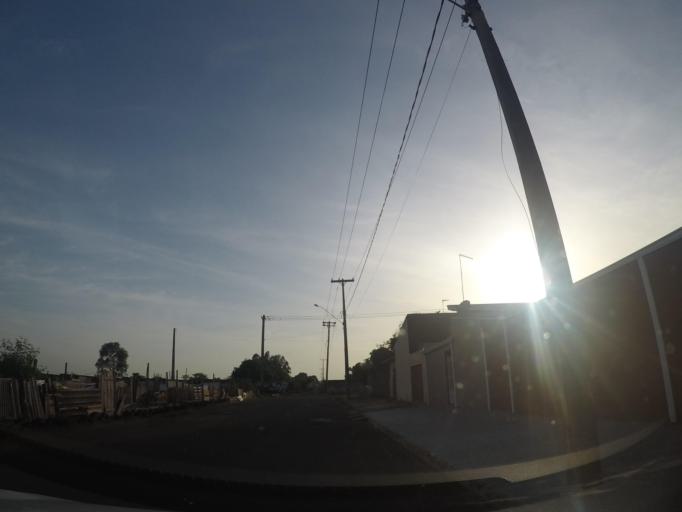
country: BR
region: Sao Paulo
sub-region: Hortolandia
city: Hortolandia
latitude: -22.8447
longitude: -47.1837
